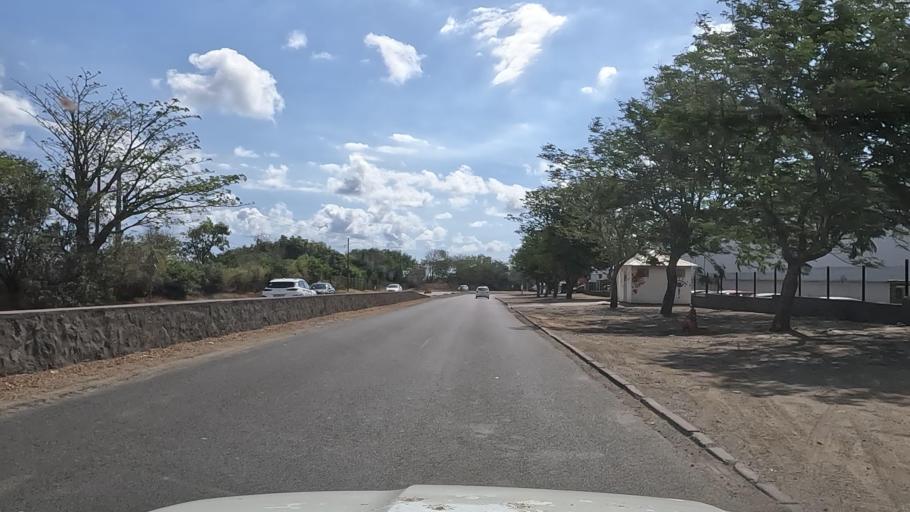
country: RE
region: Reunion
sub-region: Reunion
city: Saint-Louis
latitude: -21.2937
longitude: 55.4057
